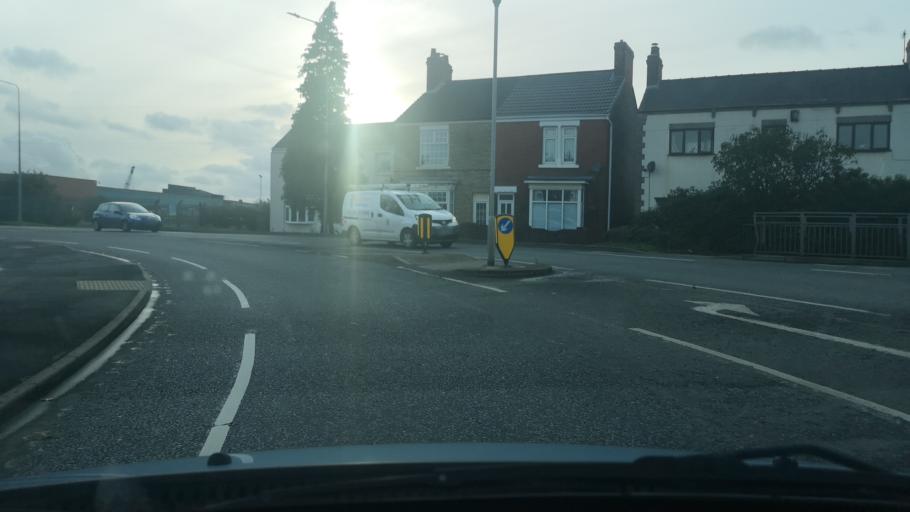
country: GB
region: England
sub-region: North Lincolnshire
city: Gunness
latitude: 53.5905
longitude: -0.7280
